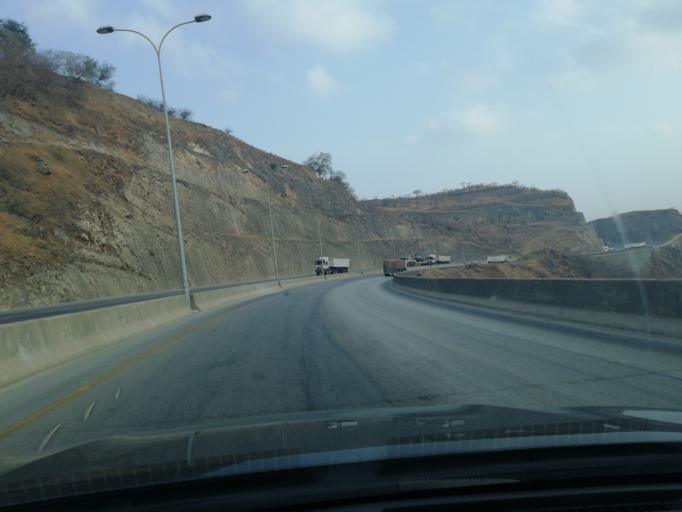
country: OM
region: Zufar
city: Salalah
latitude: 17.1387
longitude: 54.1343
